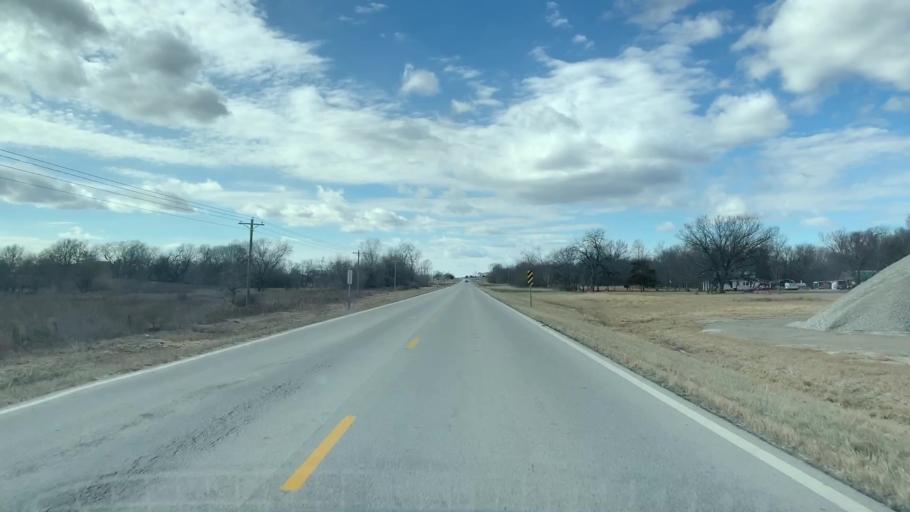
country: US
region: Kansas
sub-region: Neosho County
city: Erie
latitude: 37.5293
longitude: -95.2895
